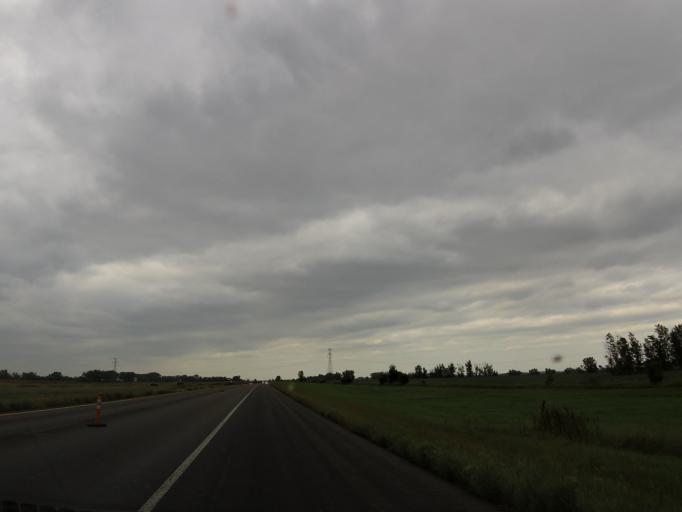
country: US
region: North Dakota
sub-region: Richland County
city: Wahpeton
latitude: 46.0947
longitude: -96.8355
